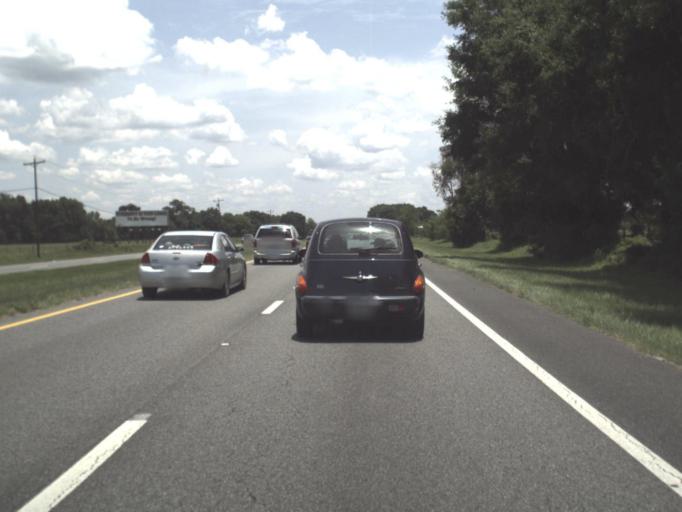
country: US
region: Florida
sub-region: Levy County
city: Manatee Road
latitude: 29.5254
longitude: -82.8848
